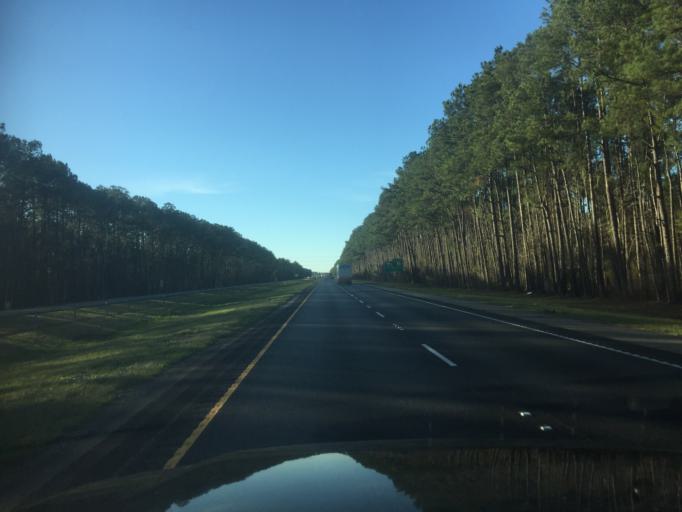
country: US
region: Louisiana
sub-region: Saint Tammany Parish
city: Lacombe
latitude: 30.3828
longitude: -89.9805
